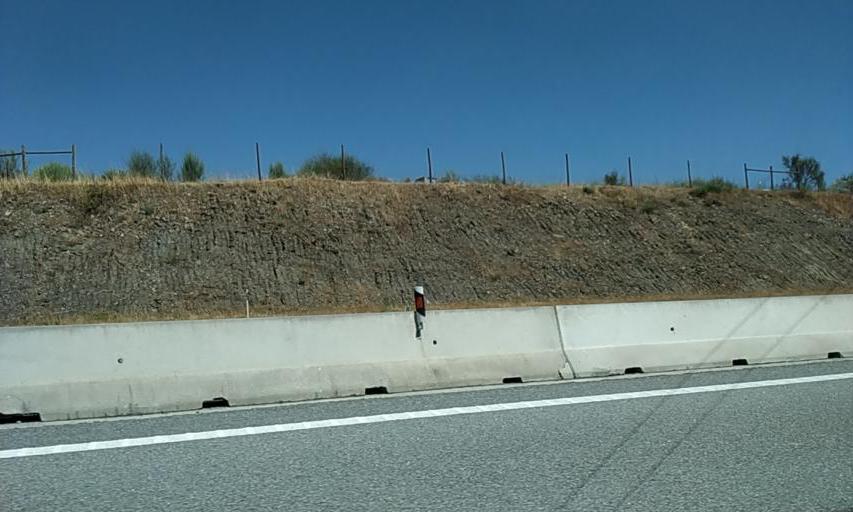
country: PT
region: Vila Real
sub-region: Murca
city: Murca
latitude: 41.4225
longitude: -7.4045
